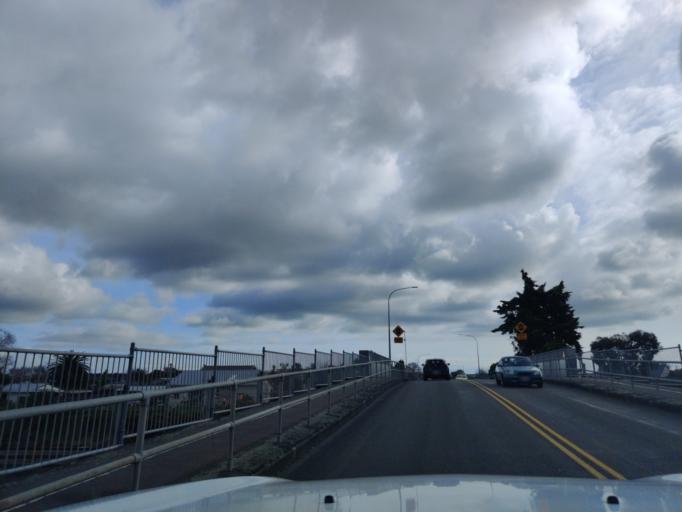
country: NZ
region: Manawatu-Wanganui
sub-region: Palmerston North City
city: Palmerston North
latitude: -40.3337
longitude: 175.6173
